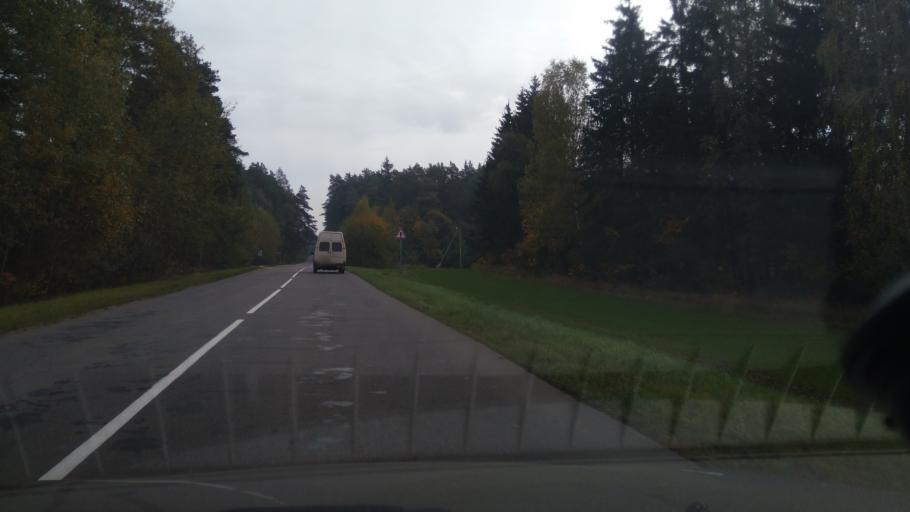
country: BY
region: Minsk
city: Rudzyensk
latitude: 53.6142
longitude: 27.7684
